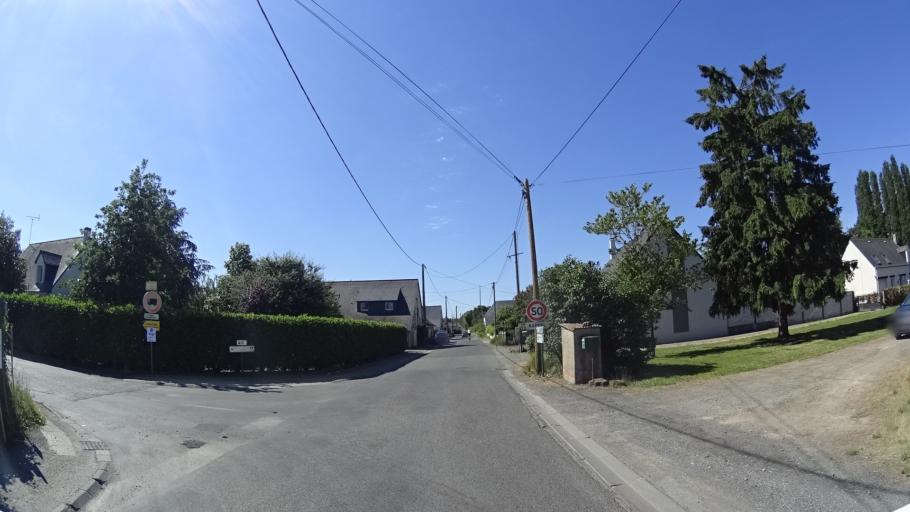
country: FR
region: Pays de la Loire
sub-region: Departement de Maine-et-Loire
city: Saint-Mathurin-sur-Loire
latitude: 47.4149
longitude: -0.3331
